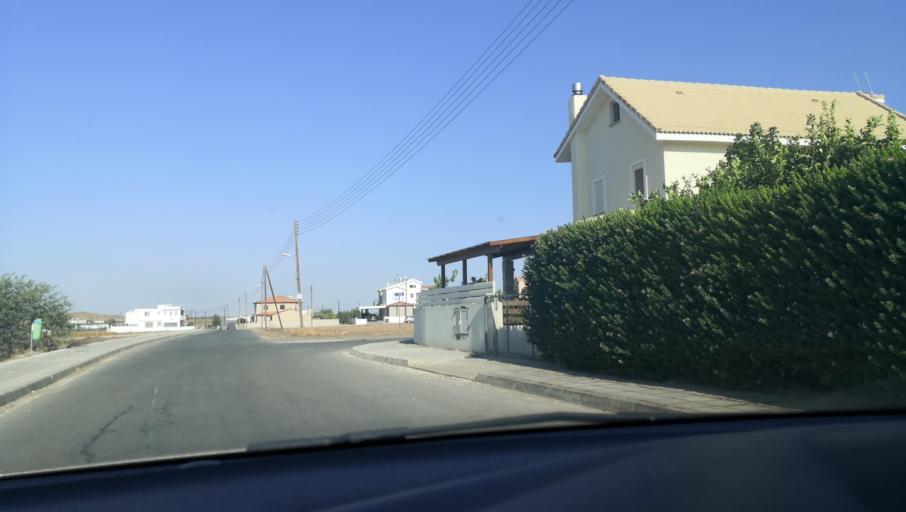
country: CY
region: Lefkosia
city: Psimolofou
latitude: 35.0614
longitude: 33.2684
